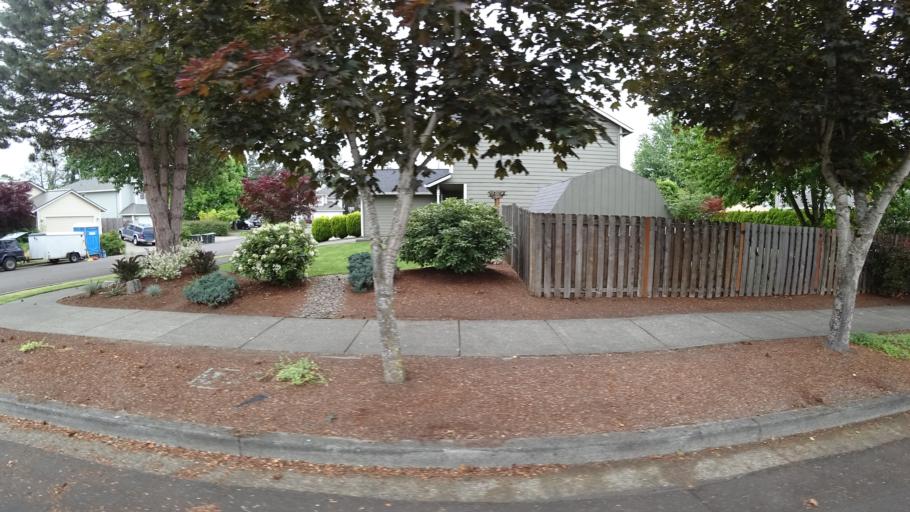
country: US
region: Oregon
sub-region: Washington County
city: Aloha
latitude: 45.5014
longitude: -122.9083
